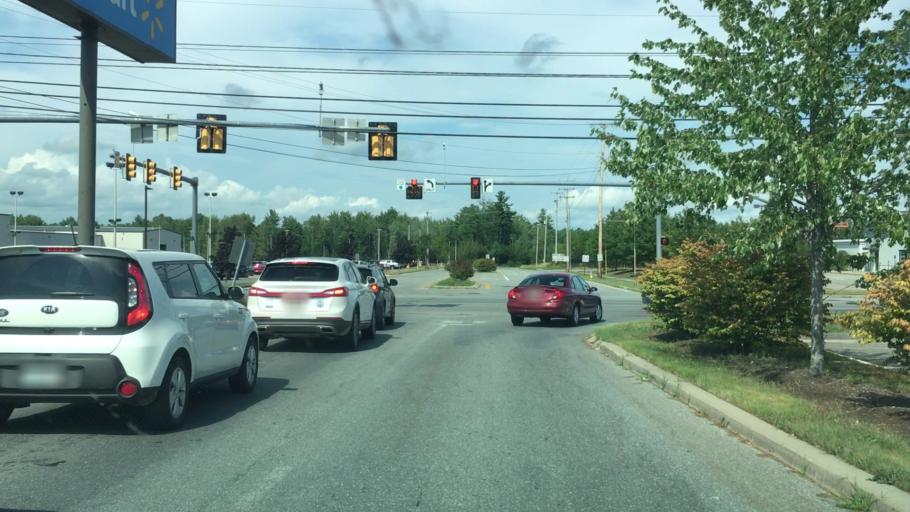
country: US
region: Maine
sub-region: Penobscot County
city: Brewer
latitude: 44.7762
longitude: -68.7338
